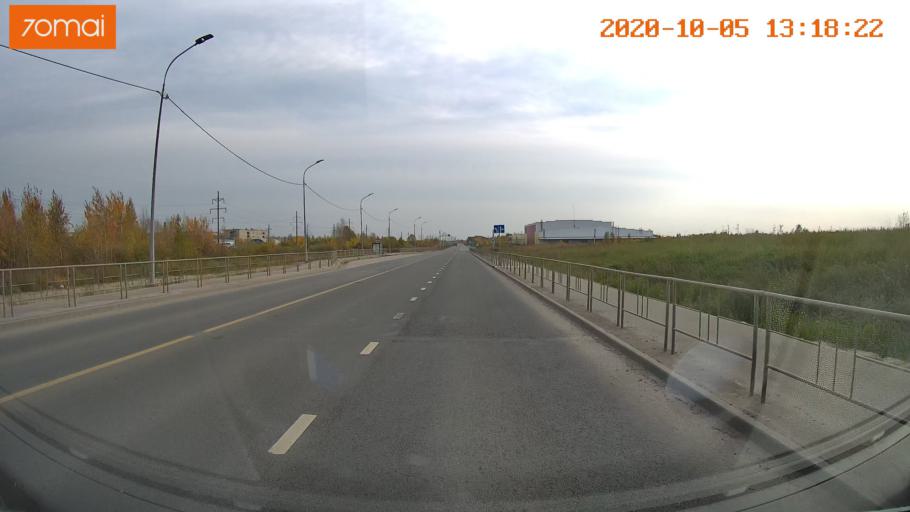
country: RU
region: Ivanovo
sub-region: Gorod Ivanovo
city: Ivanovo
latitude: 56.9778
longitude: 40.9195
